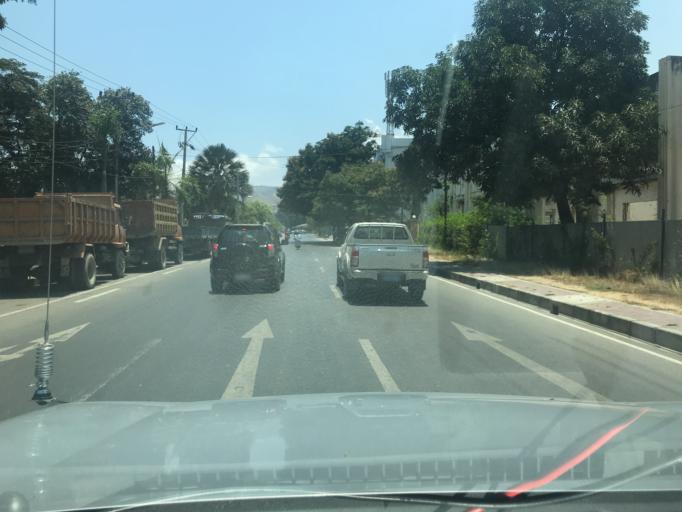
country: TL
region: Dili
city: Dili
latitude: -8.5541
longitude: 125.5724
